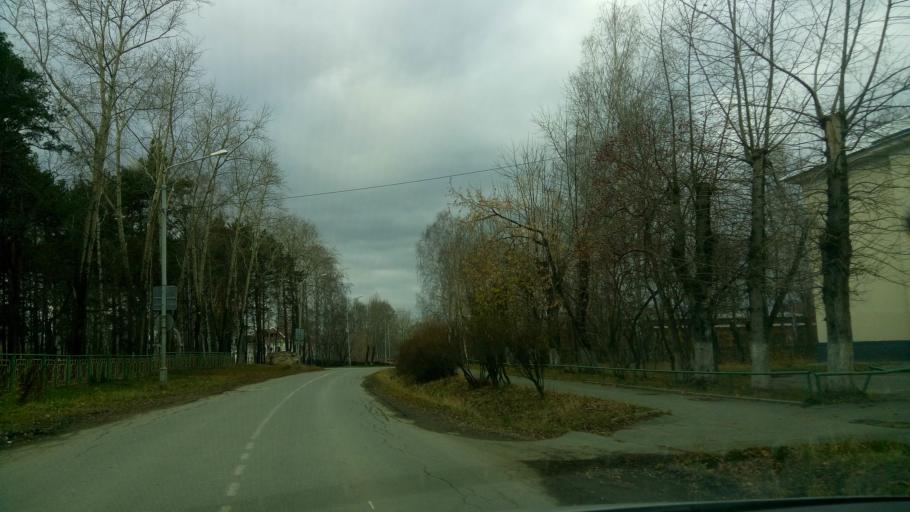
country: RU
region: Sverdlovsk
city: Sredneuralsk
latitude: 56.9889
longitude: 60.4689
